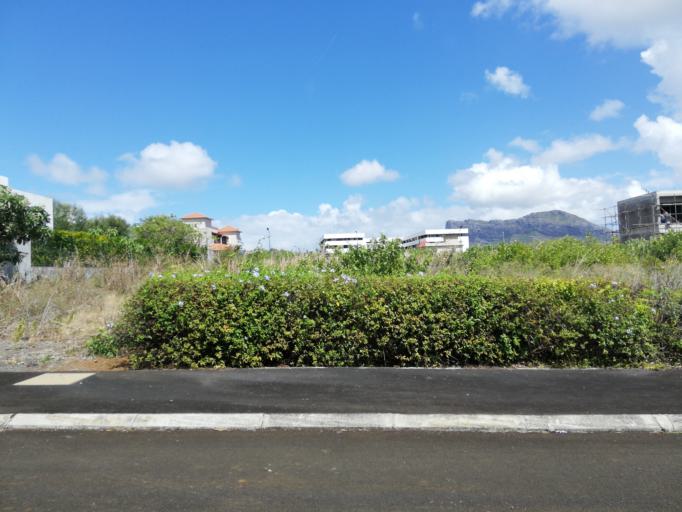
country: MU
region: Plaines Wilhems
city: Ebene
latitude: -20.2383
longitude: 57.4864
